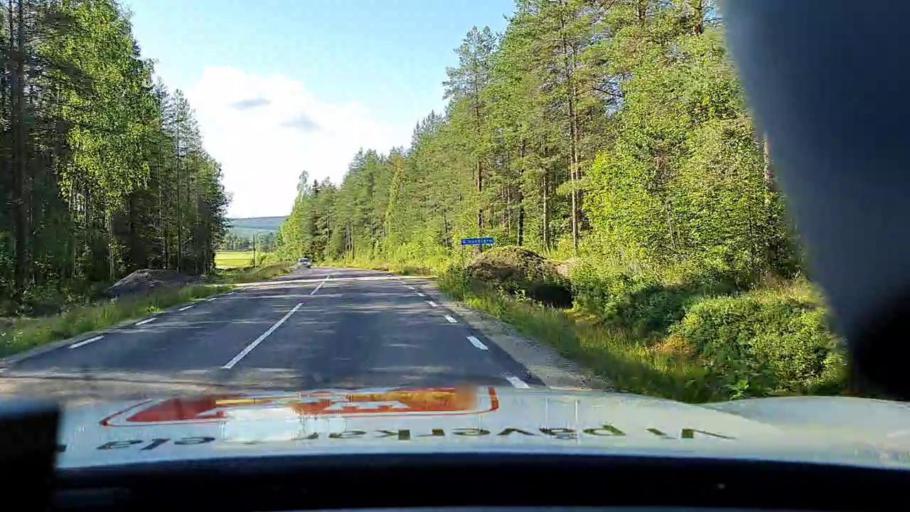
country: SE
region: Norrbotten
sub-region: Overkalix Kommun
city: OEverkalix
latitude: 66.2583
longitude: 22.8551
